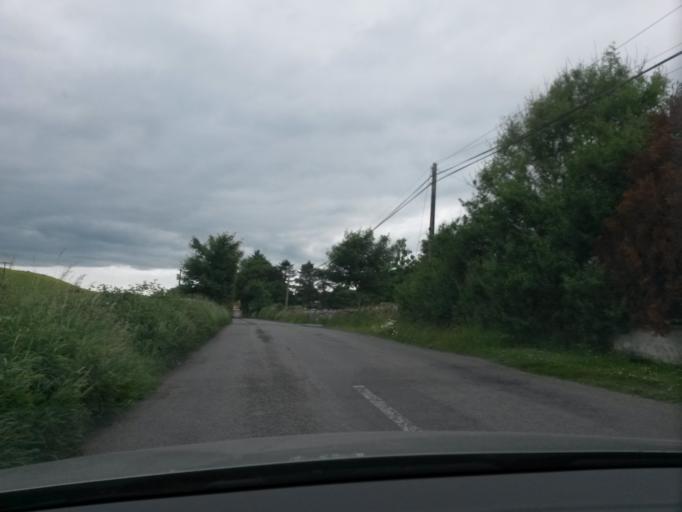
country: IE
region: Munster
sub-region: An Clar
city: Ennis
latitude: 52.9866
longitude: -9.1451
